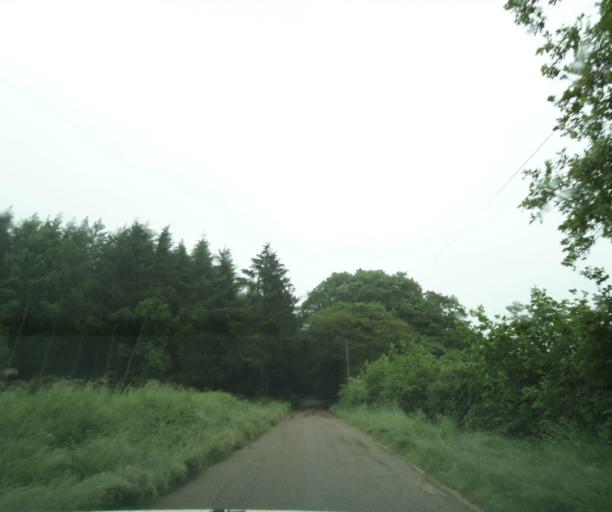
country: FR
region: Bourgogne
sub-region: Departement de Saone-et-Loire
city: Charolles
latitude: 46.4030
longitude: 4.3570
